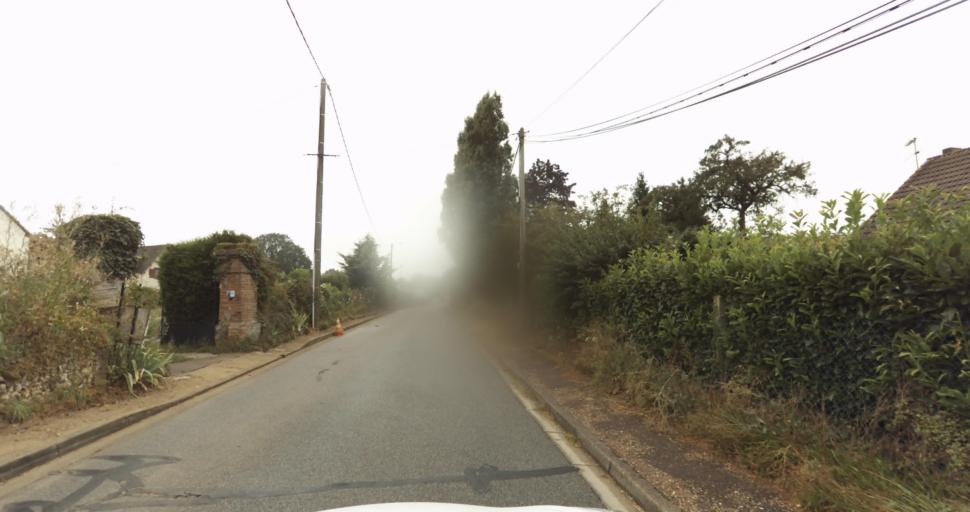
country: FR
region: Haute-Normandie
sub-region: Departement de l'Eure
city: Normanville
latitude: 49.0972
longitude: 1.1498
